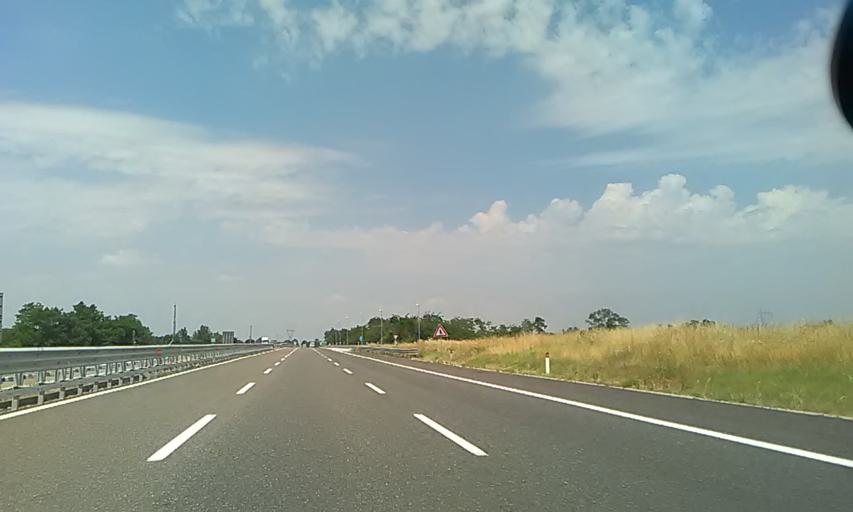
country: IT
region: Piedmont
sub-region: Provincia di Alessandria
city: Predosa
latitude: 44.7614
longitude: 8.6418
